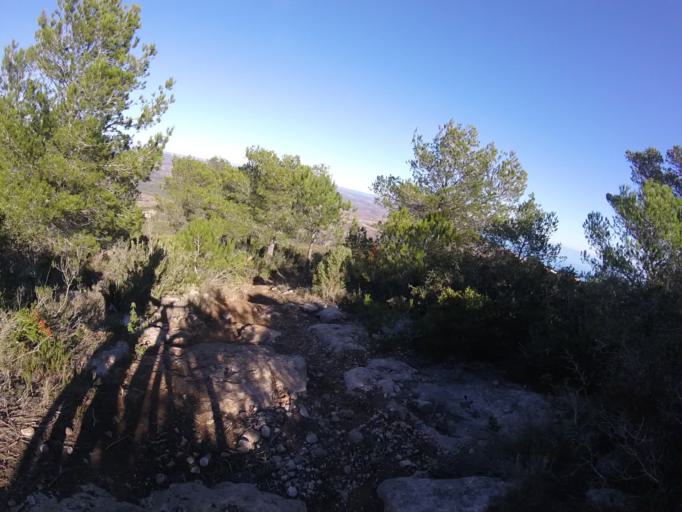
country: ES
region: Valencia
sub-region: Provincia de Castello
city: Orpesa/Oropesa del Mar
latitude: 40.1013
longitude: 0.1125
